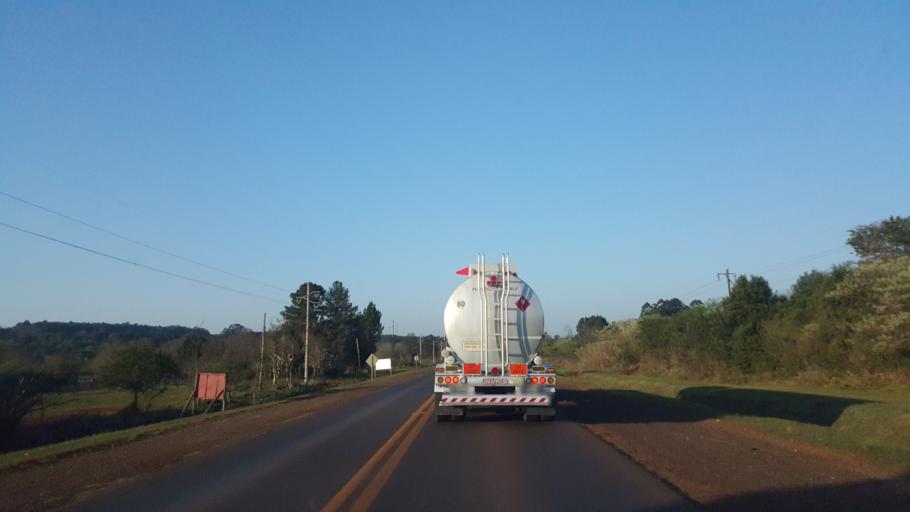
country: AR
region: Misiones
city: Jardin America
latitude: -27.0325
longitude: -55.2214
